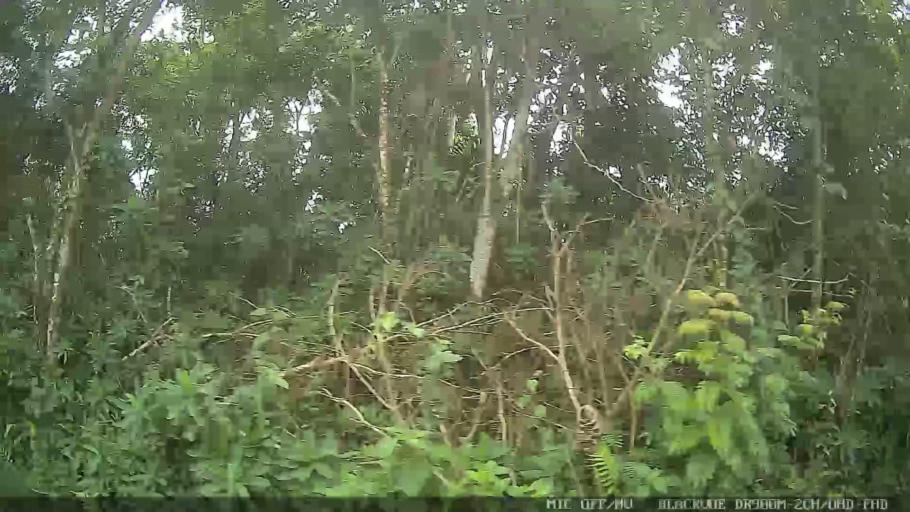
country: BR
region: Sao Paulo
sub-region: Santa Isabel
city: Santa Isabel
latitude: -23.3583
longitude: -46.2300
